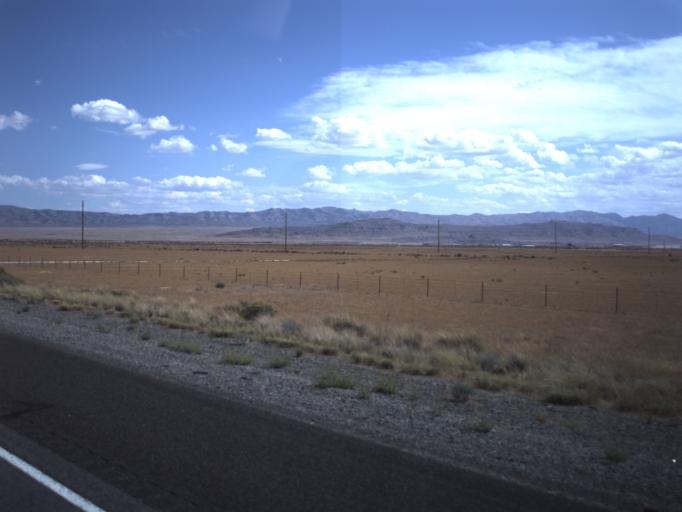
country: US
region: Utah
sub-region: Tooele County
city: Grantsville
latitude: 40.7251
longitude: -113.1471
